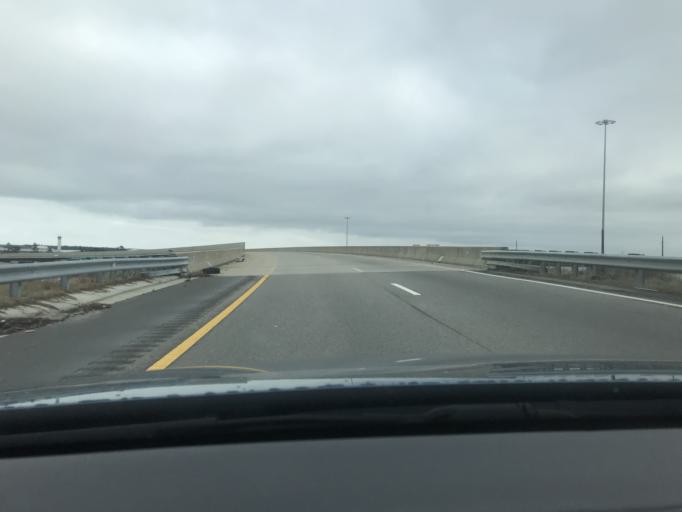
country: US
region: North Carolina
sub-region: Cumberland County
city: Spring Lake
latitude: 35.1202
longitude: -78.9399
